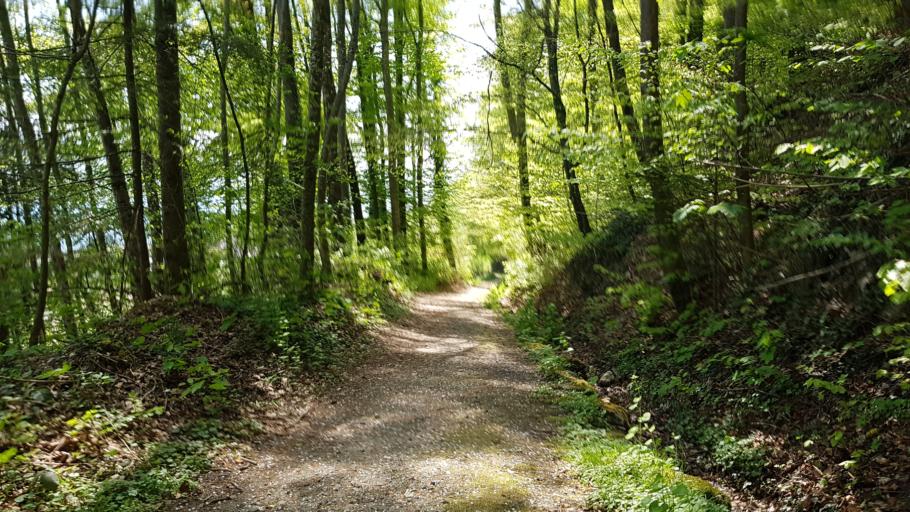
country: CH
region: Aargau
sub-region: Bezirk Lenzburg
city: Boniswil
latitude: 47.2920
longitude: 8.1904
